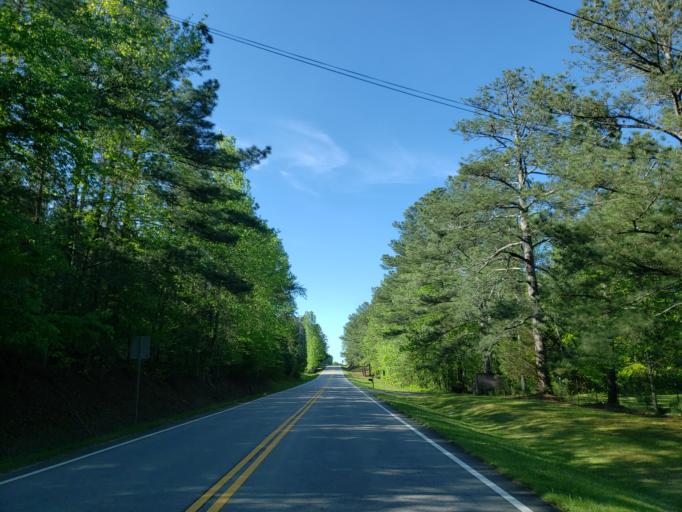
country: US
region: Georgia
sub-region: Haralson County
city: Tallapoosa
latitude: 33.8976
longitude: -85.3121
